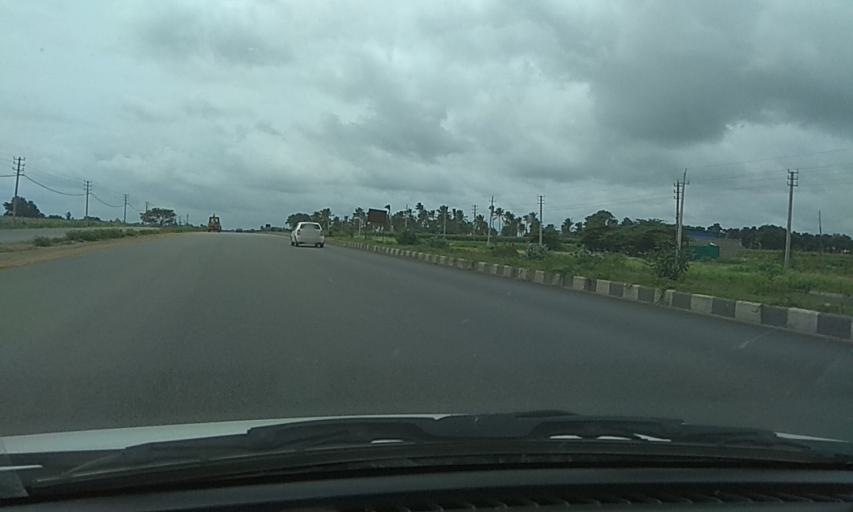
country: IN
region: Karnataka
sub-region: Davanagere
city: Mayakonda
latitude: 14.3561
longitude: 76.1994
